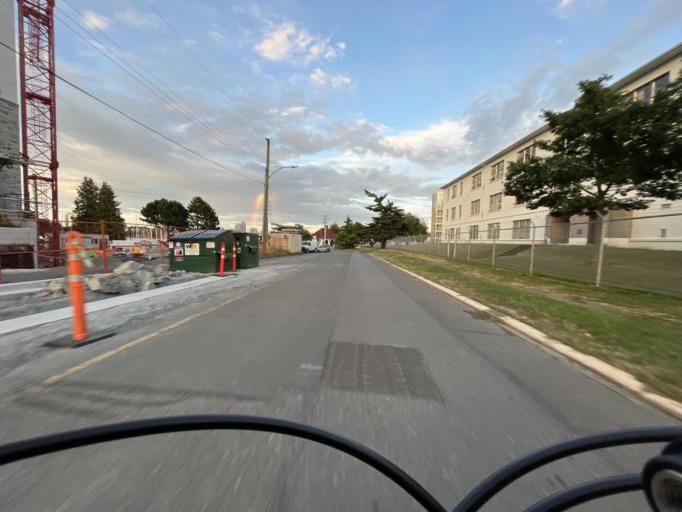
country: CA
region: British Columbia
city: Victoria
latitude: 48.4261
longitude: -123.3995
